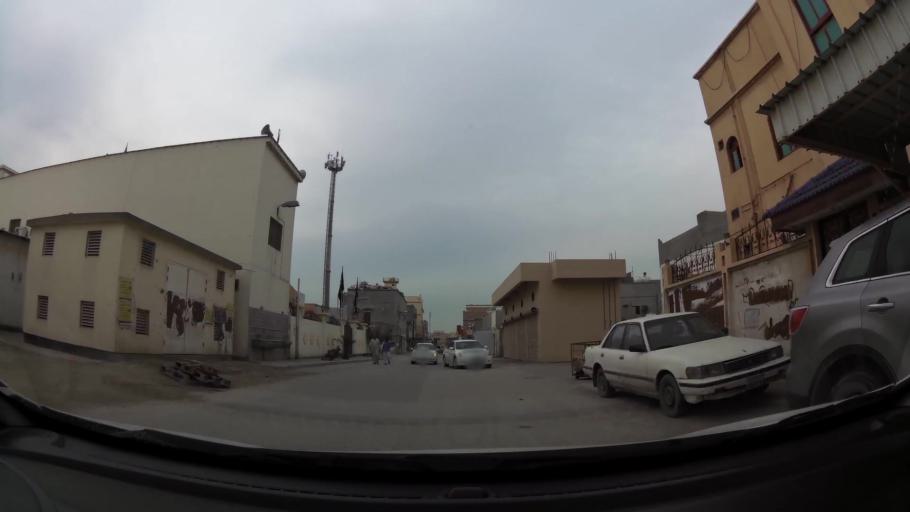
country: BH
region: Northern
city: Sitrah
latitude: 26.1336
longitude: 50.6136
